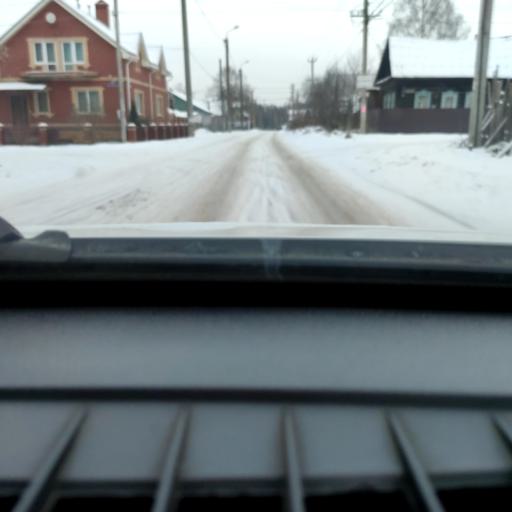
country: RU
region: Perm
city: Perm
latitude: 58.0995
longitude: 56.3679
